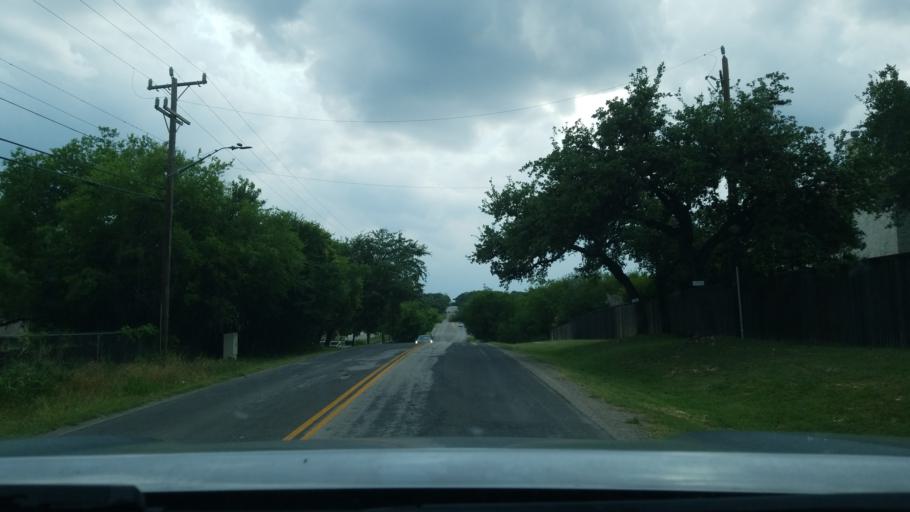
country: US
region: Texas
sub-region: Bexar County
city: Leon Valley
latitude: 29.5447
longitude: -98.6023
